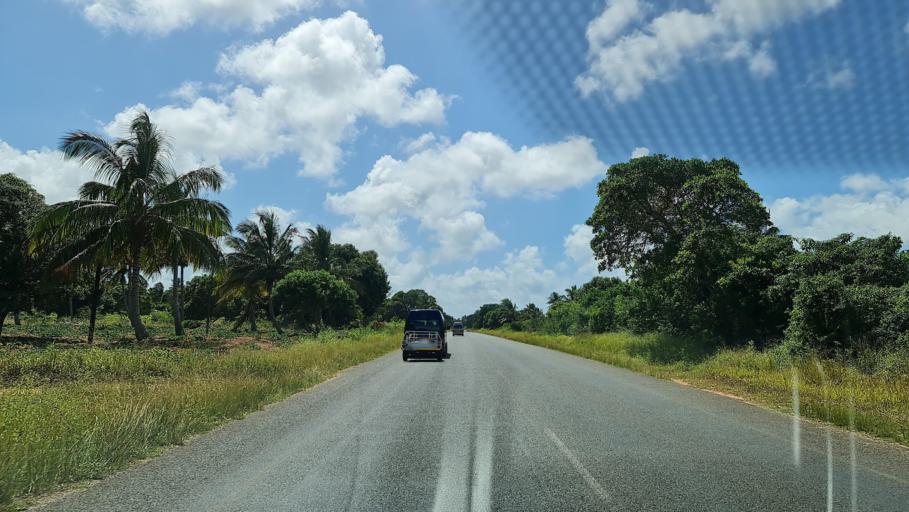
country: MZ
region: Inhambane
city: Maxixe
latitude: -24.5405
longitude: 34.9248
